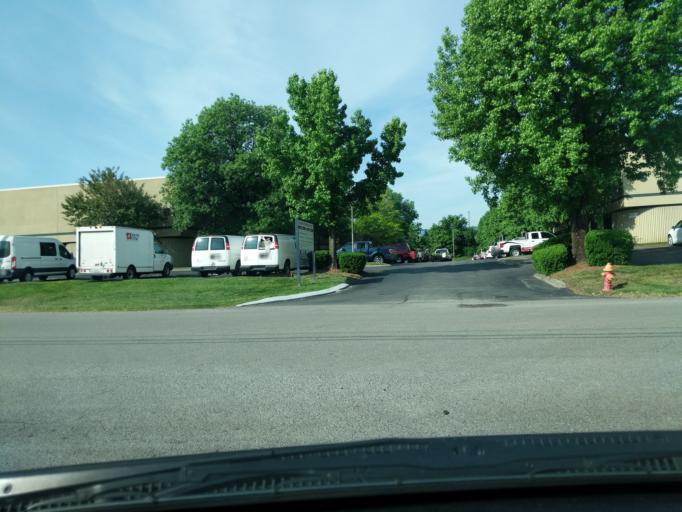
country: US
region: Tennessee
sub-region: Davidson County
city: Oak Hill
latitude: 36.0908
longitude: -86.6899
